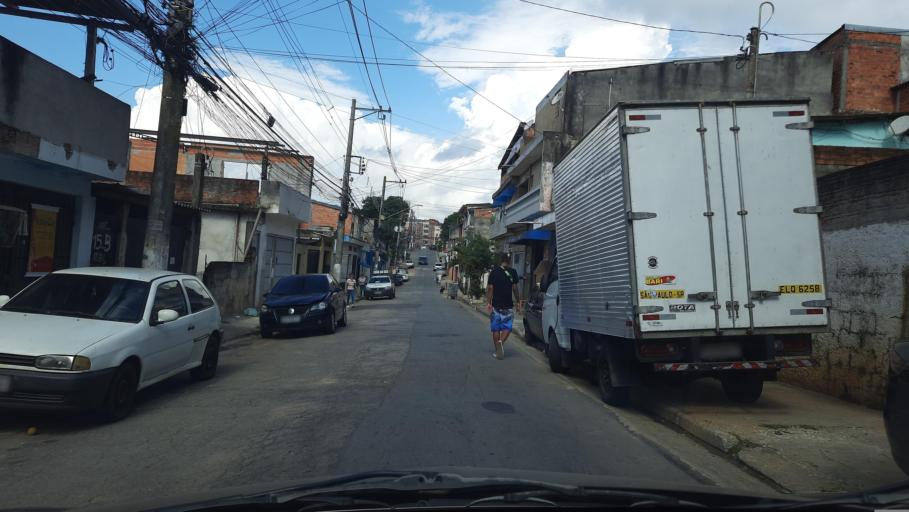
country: BR
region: Sao Paulo
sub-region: Caieiras
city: Caieiras
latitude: -23.4491
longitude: -46.7191
